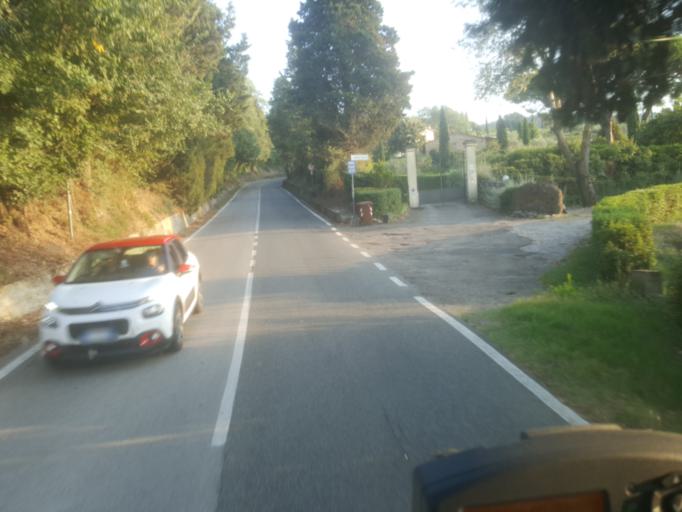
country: IT
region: Tuscany
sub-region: Province of Florence
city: Montaione
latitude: 43.5421
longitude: 10.9273
